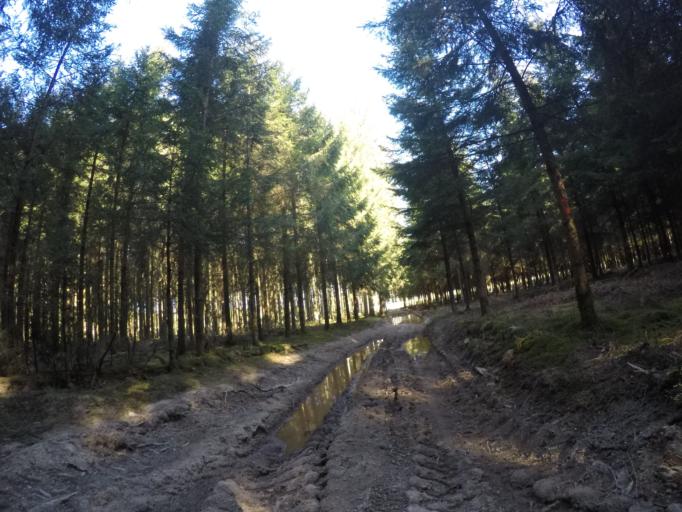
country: BE
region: Wallonia
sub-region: Province du Luxembourg
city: Leglise
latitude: 49.7966
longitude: 5.5829
